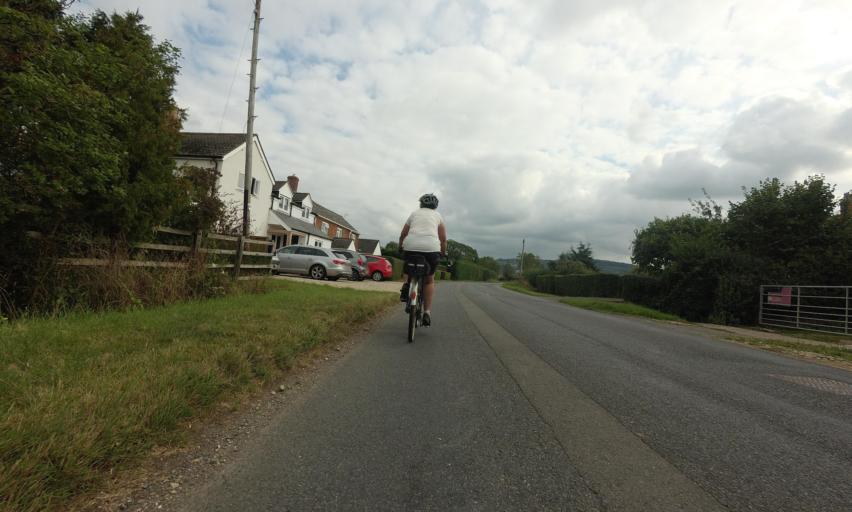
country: GB
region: England
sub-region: Gloucestershire
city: Winchcombe
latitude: 51.9880
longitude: -1.9997
